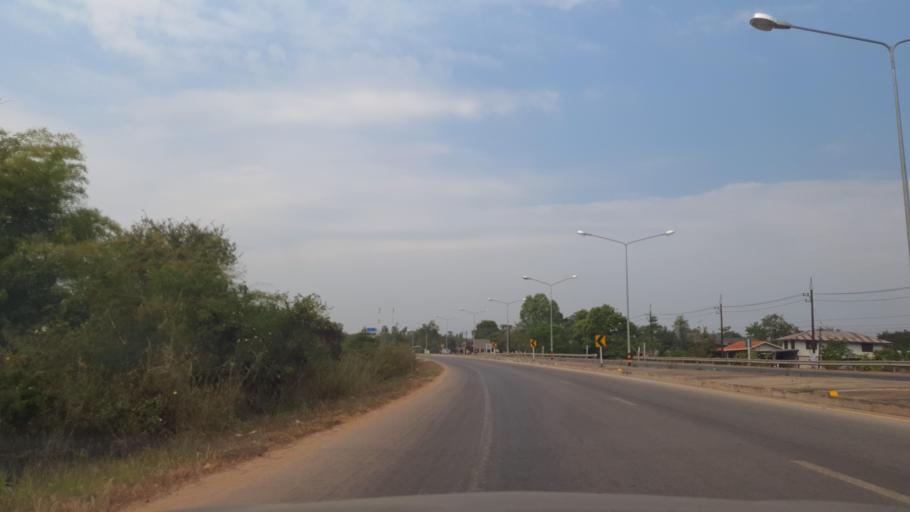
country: TH
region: Changwat Bueng Kan
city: Si Wilai
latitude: 18.3037
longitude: 103.8140
